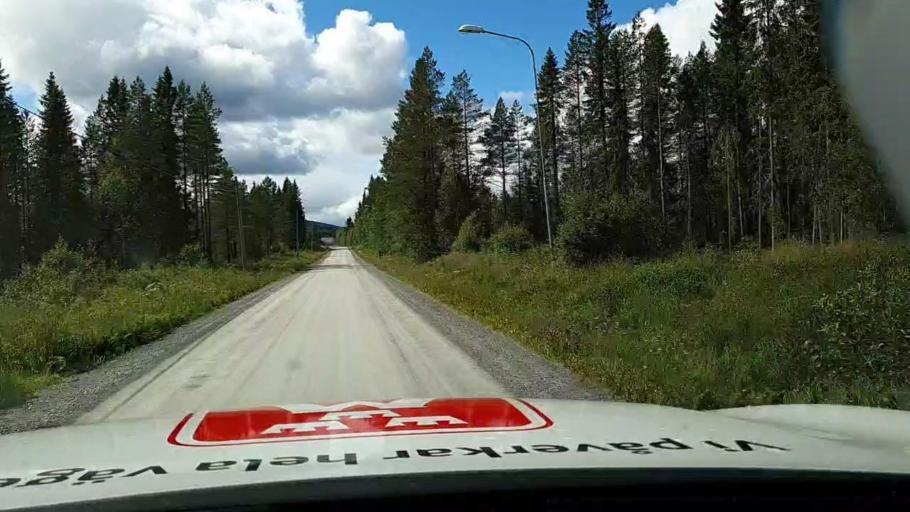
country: SE
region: Jaemtland
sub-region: Krokoms Kommun
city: Valla
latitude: 63.6973
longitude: 13.6219
